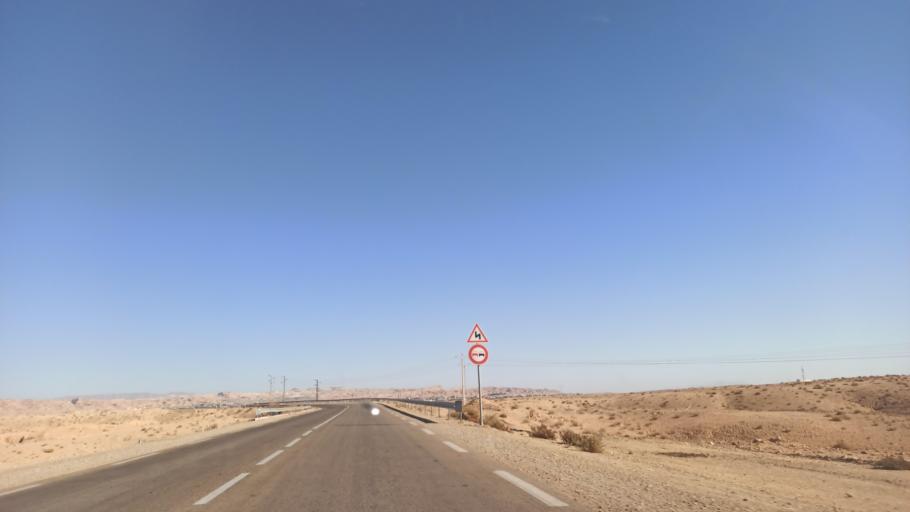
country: TN
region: Gafsa
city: Al Metlaoui
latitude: 34.2978
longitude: 8.3576
